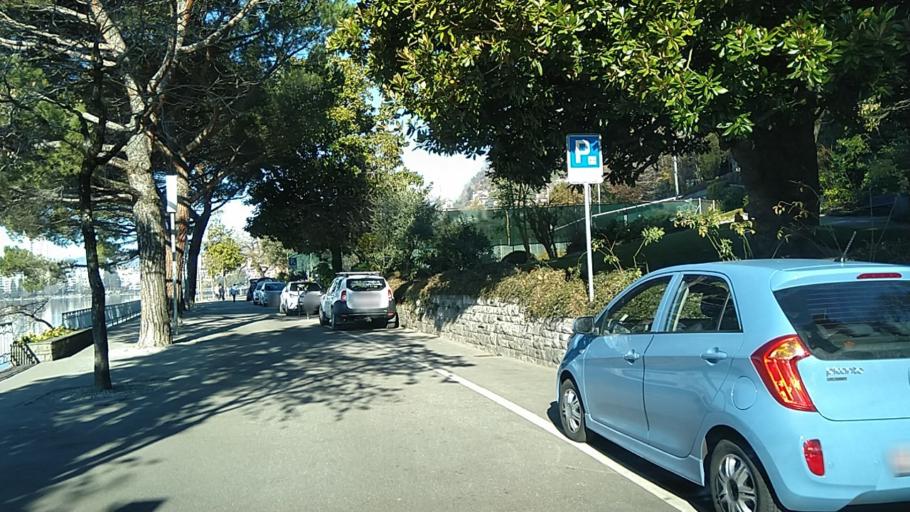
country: CH
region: Vaud
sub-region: Riviera-Pays-d'Enhaut District
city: Montreux
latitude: 46.4244
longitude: 6.9236
